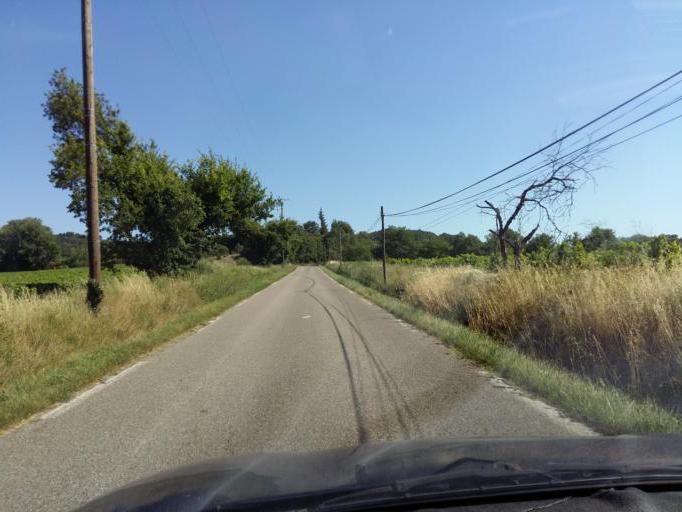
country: FR
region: Provence-Alpes-Cote d'Azur
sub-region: Departement du Vaucluse
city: Valreas
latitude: 44.3693
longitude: 4.9879
